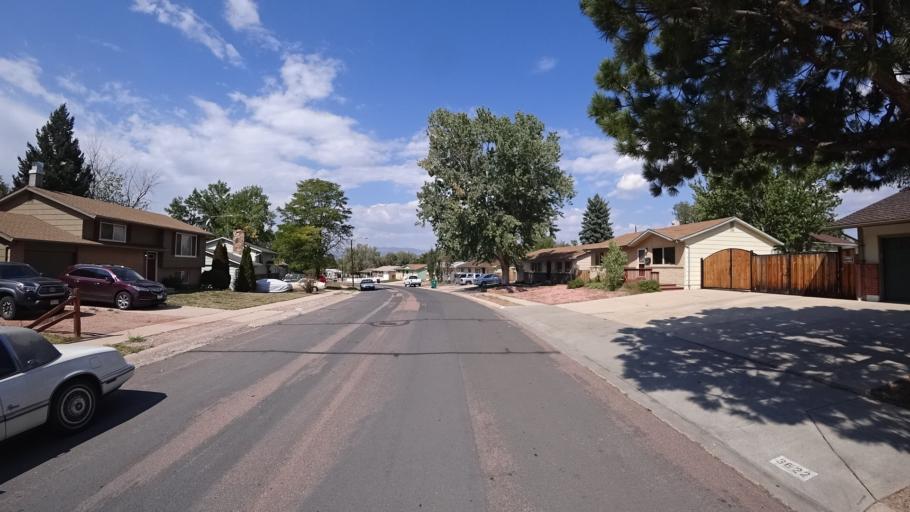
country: US
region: Colorado
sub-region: El Paso County
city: Colorado Springs
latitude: 38.8299
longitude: -104.7648
